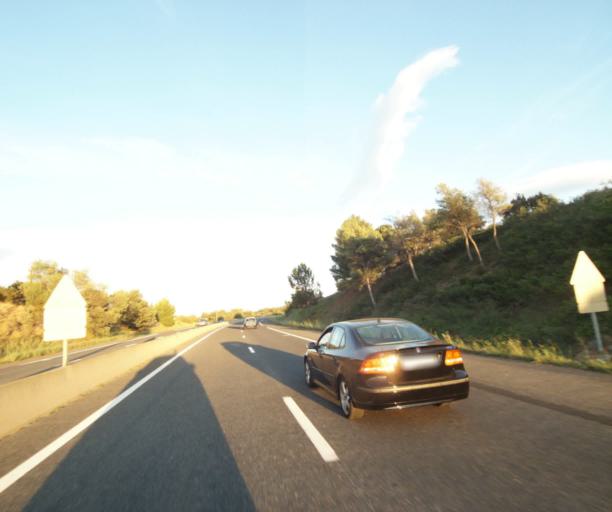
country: FR
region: Languedoc-Roussillon
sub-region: Departement des Pyrenees-Orientales
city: Argelers
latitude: 42.5351
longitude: 3.0391
